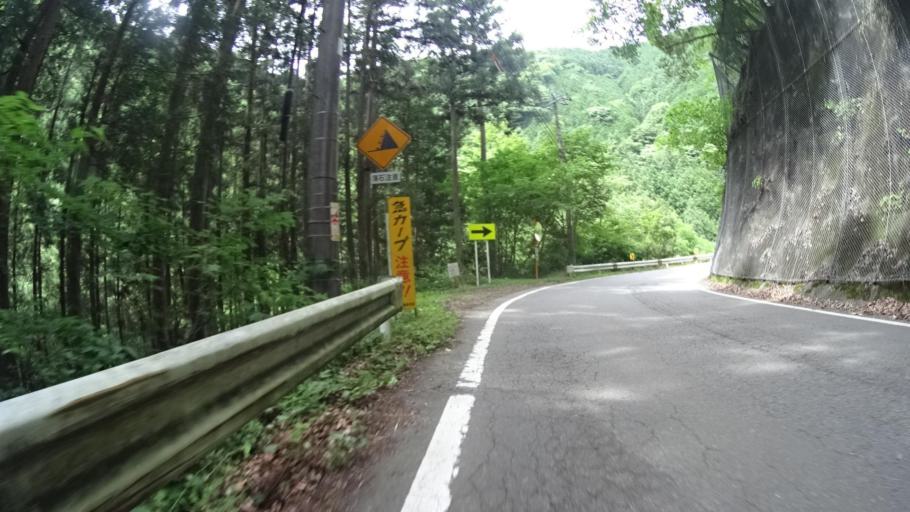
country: JP
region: Yamanashi
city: Uenohara
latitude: 35.6807
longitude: 139.0532
